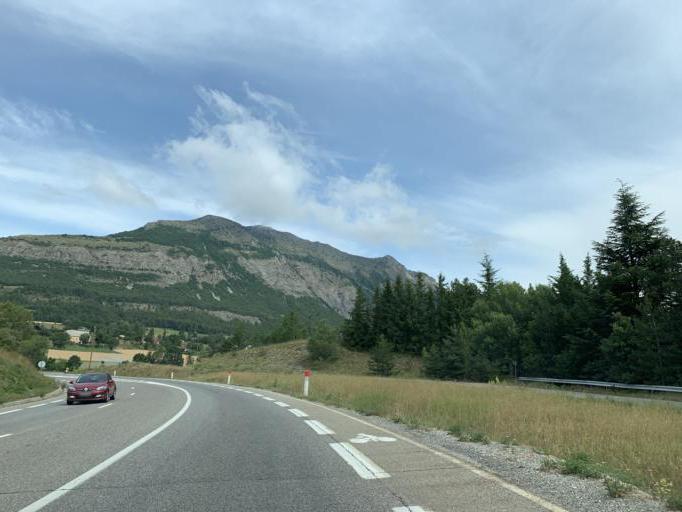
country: FR
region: Provence-Alpes-Cote d'Azur
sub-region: Departement des Hautes-Alpes
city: Gap
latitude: 44.5519
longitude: 6.0358
